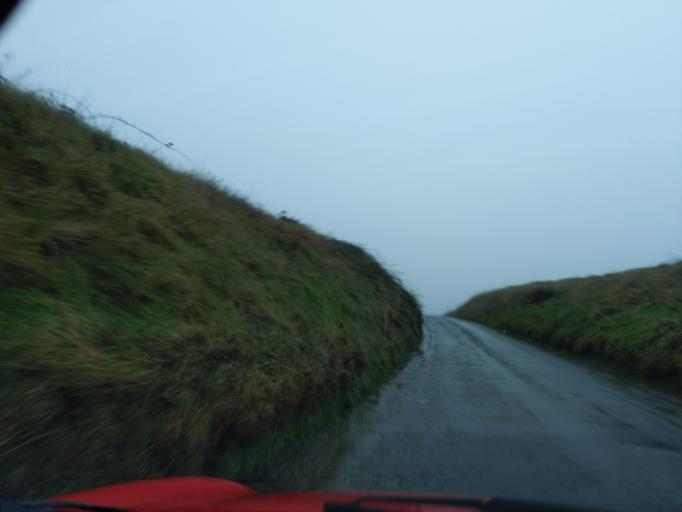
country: GB
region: England
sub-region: Cornwall
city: Camelford
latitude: 50.6505
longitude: -4.7006
